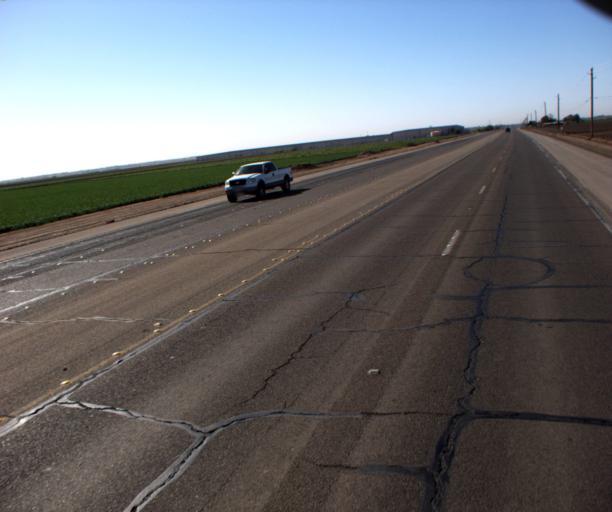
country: US
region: Arizona
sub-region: Yuma County
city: San Luis
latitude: 32.5359
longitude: -114.7870
